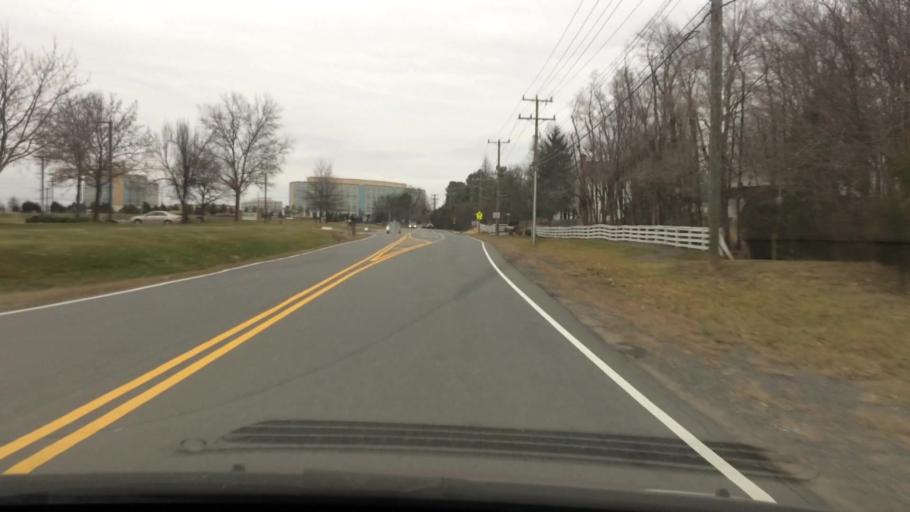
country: US
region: Virginia
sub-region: Fairfax County
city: Chantilly
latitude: 38.9070
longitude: -77.4188
